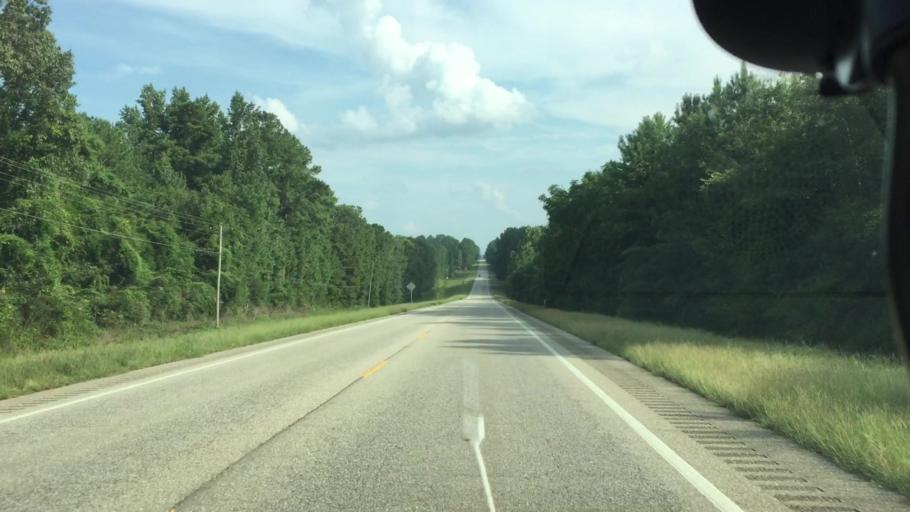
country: US
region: Alabama
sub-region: Pike County
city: Troy
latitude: 31.6712
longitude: -85.9555
